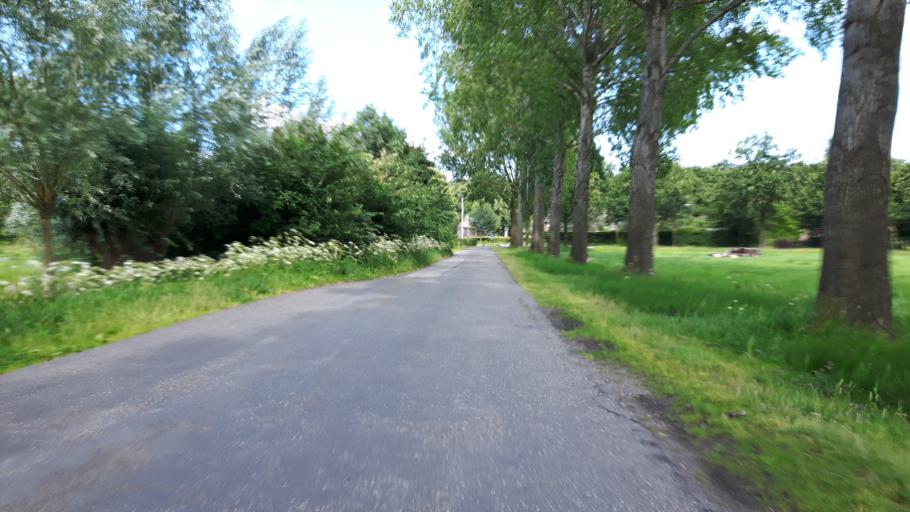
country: NL
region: Utrecht
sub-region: Stichtse Vecht
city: Spechtenkamp
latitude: 52.1188
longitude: 4.9810
